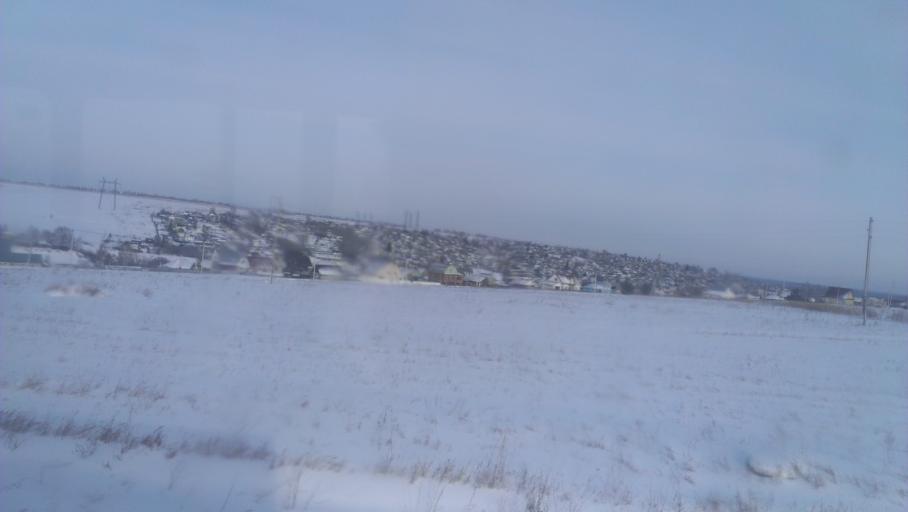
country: RU
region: Altai Krai
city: Gon'ba
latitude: 53.4127
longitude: 83.5567
